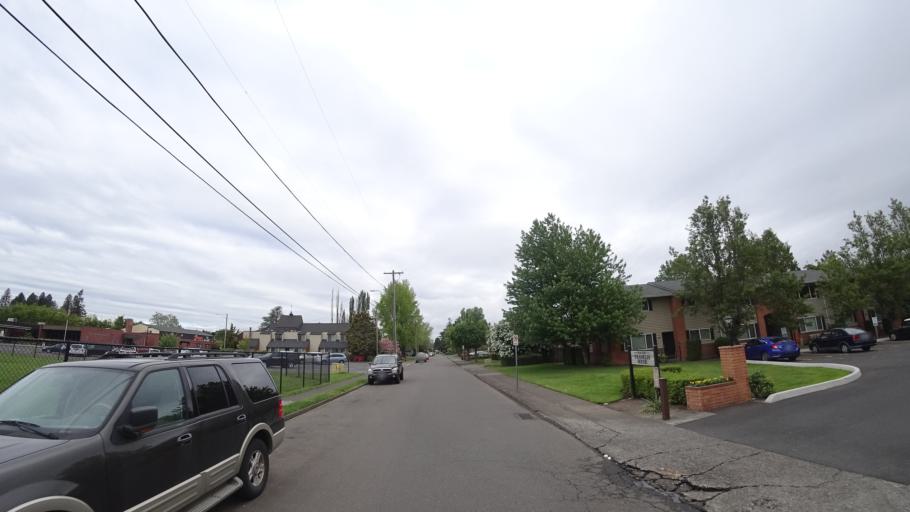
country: US
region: Oregon
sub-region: Washington County
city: Beaverton
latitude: 45.4818
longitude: -122.8019
